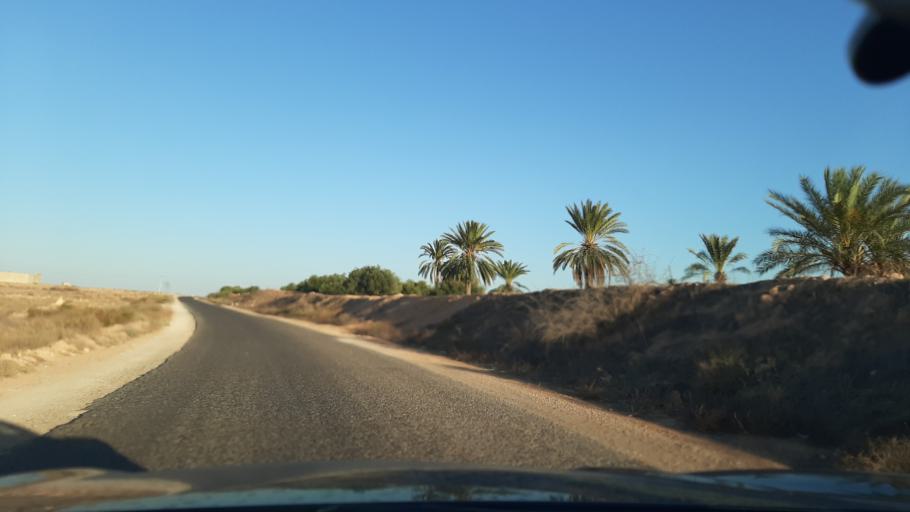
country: TN
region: Qabis
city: Matmata
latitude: 33.6245
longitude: 10.1353
